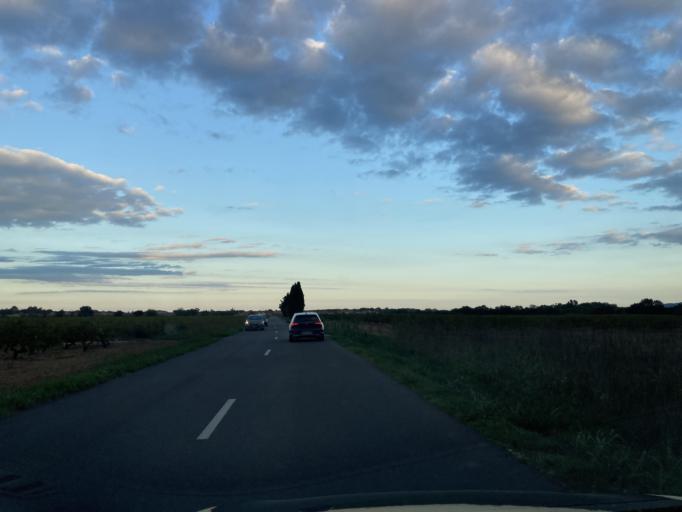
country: FR
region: Languedoc-Roussillon
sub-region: Departement des Pyrenees-Orientales
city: Banyuls-dels-Aspres
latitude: 42.5616
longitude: 2.8878
